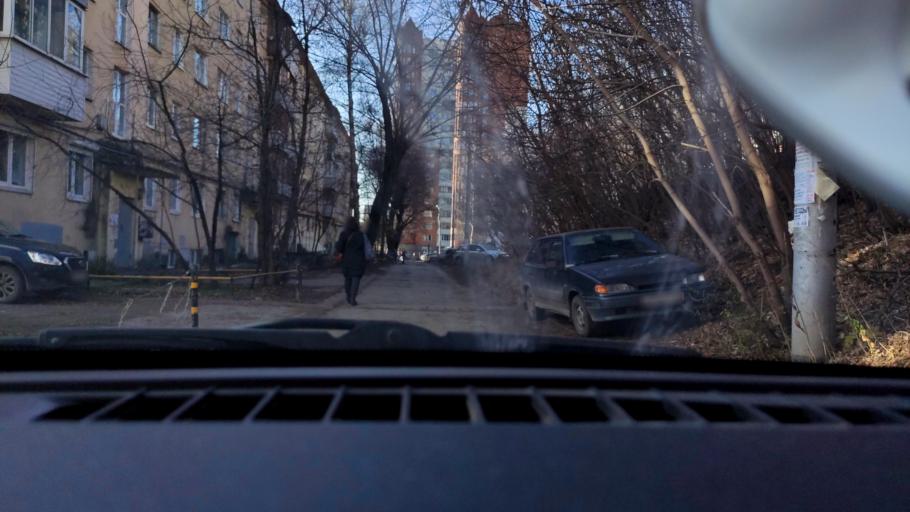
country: RU
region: Perm
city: Perm
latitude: 58.0073
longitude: 56.2033
